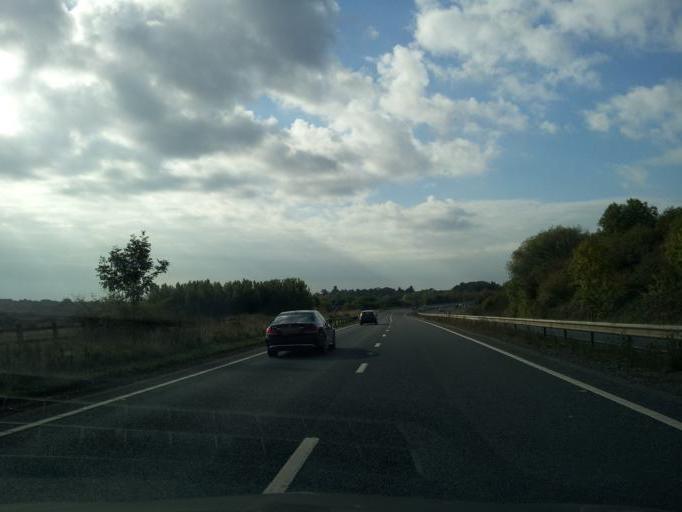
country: GB
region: England
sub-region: Northamptonshire
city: Blisworth
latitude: 52.1918
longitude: -0.9442
